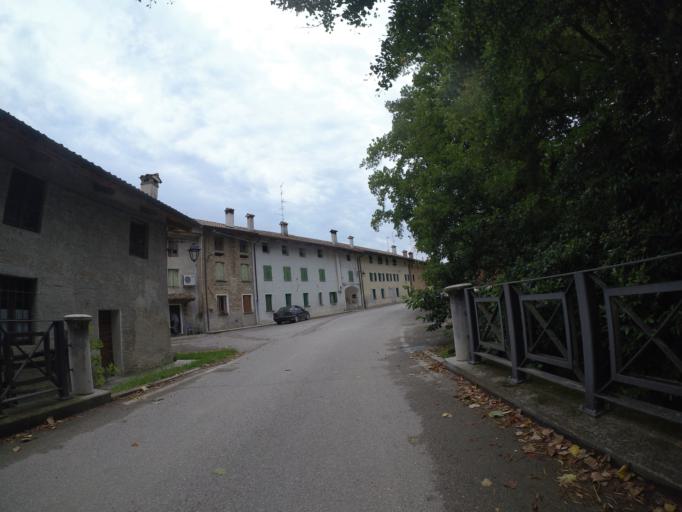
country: IT
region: Friuli Venezia Giulia
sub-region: Provincia di Udine
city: Rivignano
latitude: 45.9043
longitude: 13.0518
